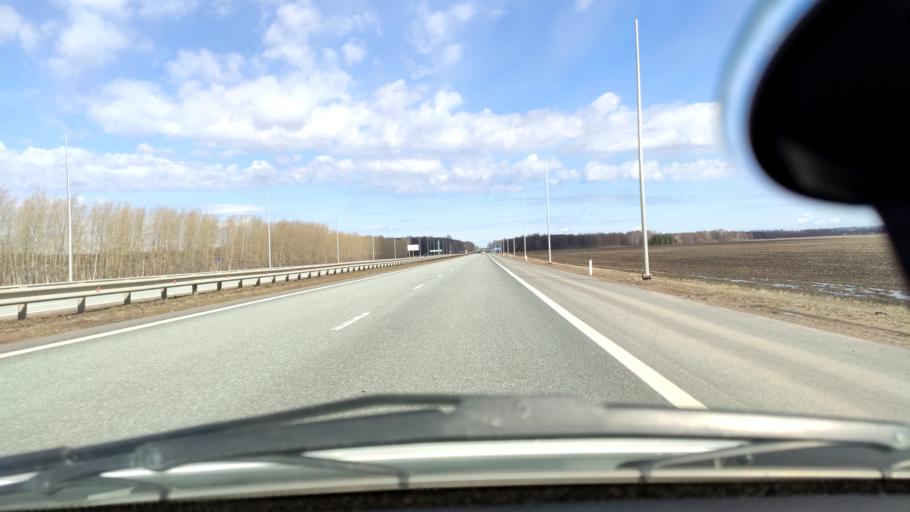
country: RU
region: Bashkortostan
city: Kabakovo
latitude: 54.4411
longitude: 55.9222
